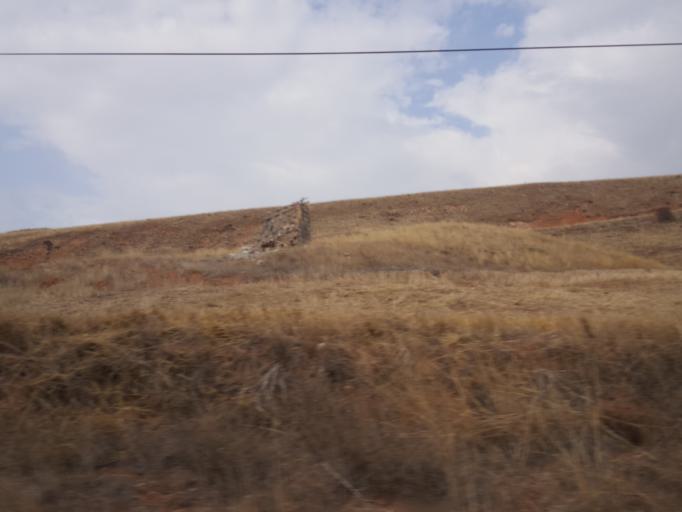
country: TR
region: Corum
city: Cemilbey
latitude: 40.2416
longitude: 35.0622
